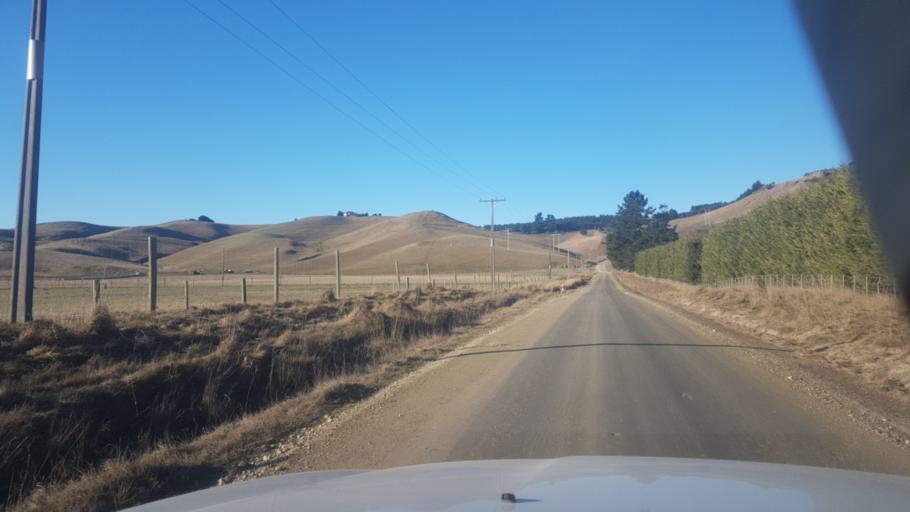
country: NZ
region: Canterbury
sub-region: Timaru District
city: Pleasant Point
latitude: -44.3436
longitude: 171.0559
